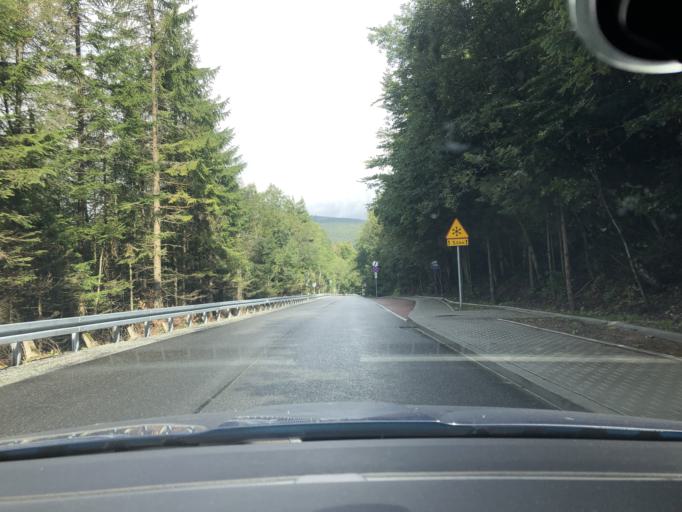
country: PL
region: Lesser Poland Voivodeship
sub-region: Powiat suski
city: Zawoja
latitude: 49.5888
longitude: 19.5827
